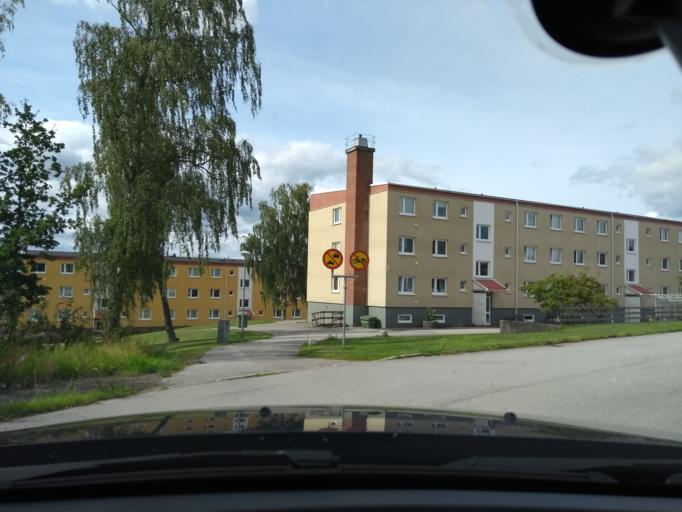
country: SE
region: Kalmar
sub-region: Vimmerby Kommun
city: Vimmerby
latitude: 57.6747
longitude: 15.8611
